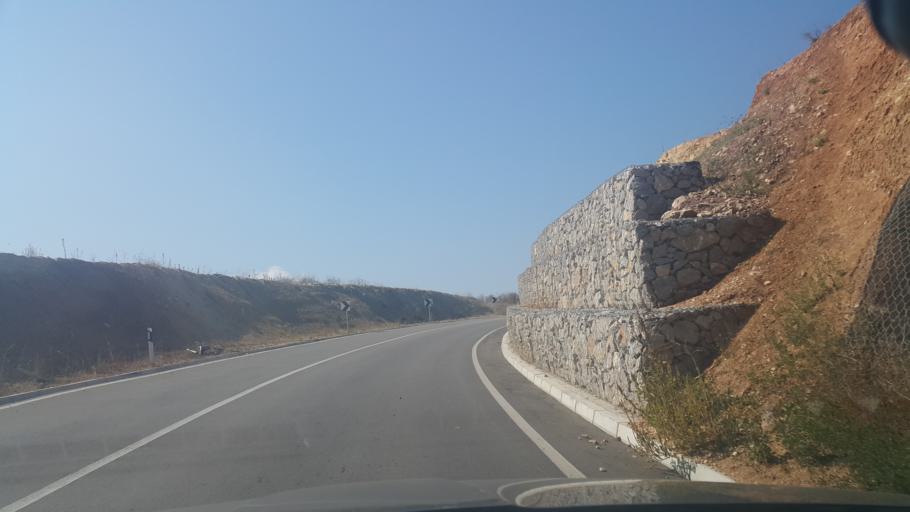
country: RS
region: Central Serbia
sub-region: Pirotski Okrug
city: Bela Palanka
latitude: 43.2293
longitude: 22.4285
